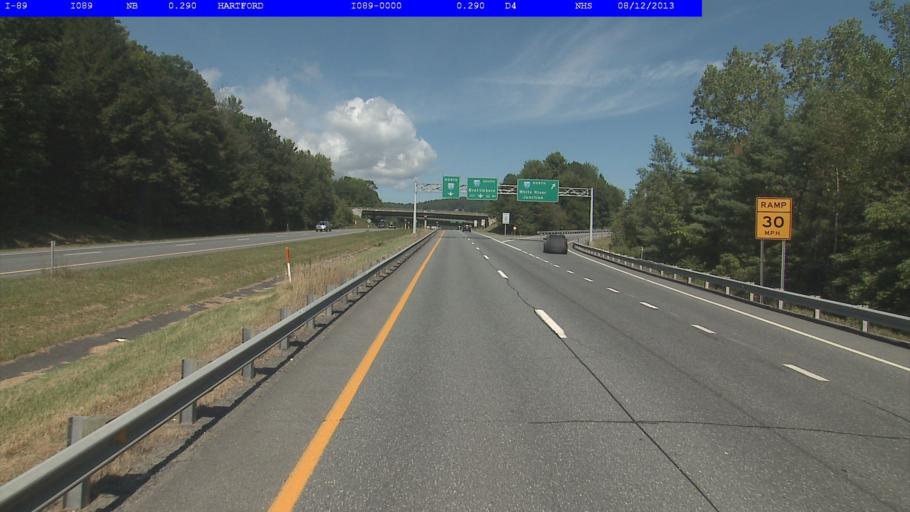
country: US
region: Vermont
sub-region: Windsor County
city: White River Junction
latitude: 43.6373
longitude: -72.3341
